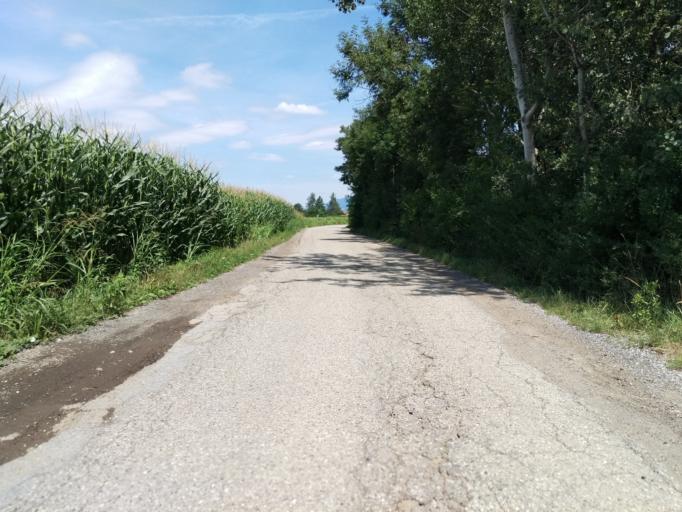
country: AT
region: Styria
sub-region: Politischer Bezirk Graz-Umgebung
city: Kalsdorf bei Graz
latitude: 46.9751
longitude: 15.4482
